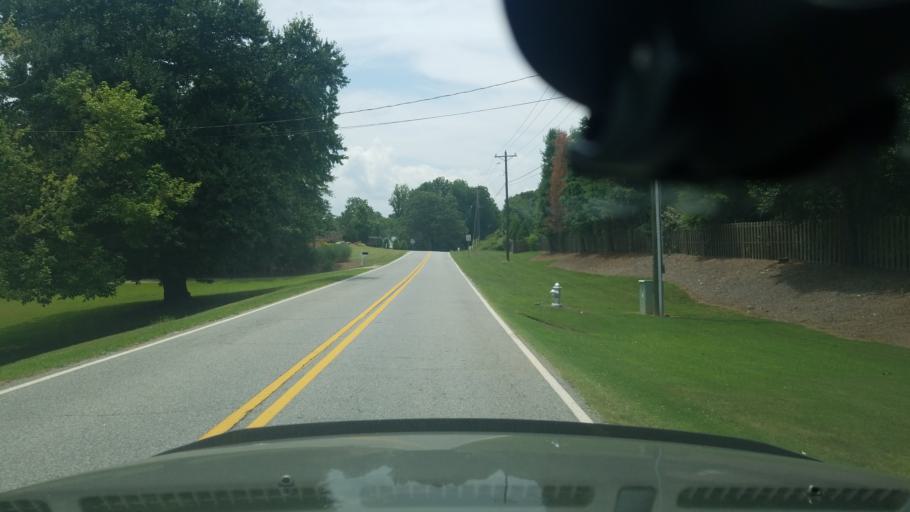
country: US
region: Georgia
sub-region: Forsyth County
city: Cumming
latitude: 34.2189
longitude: -84.1997
